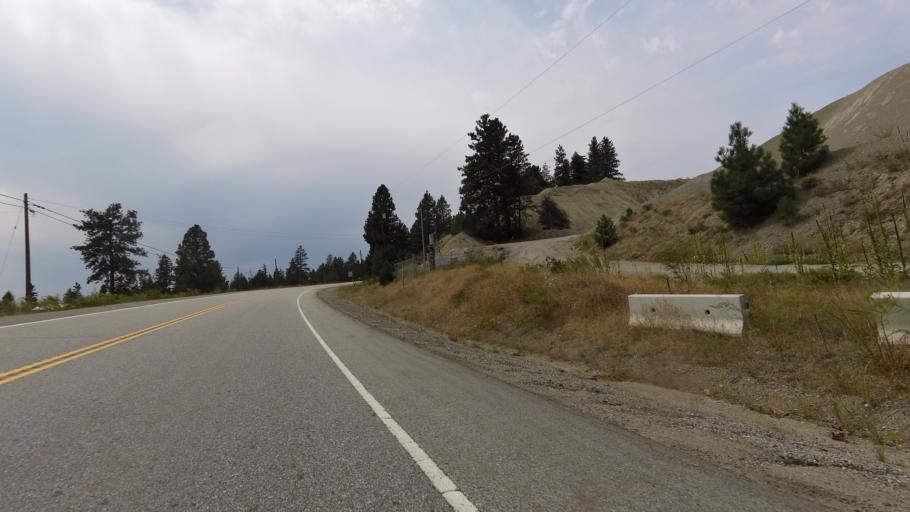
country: US
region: Washington
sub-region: Okanogan County
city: Oroville
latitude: 49.0054
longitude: -119.3139
